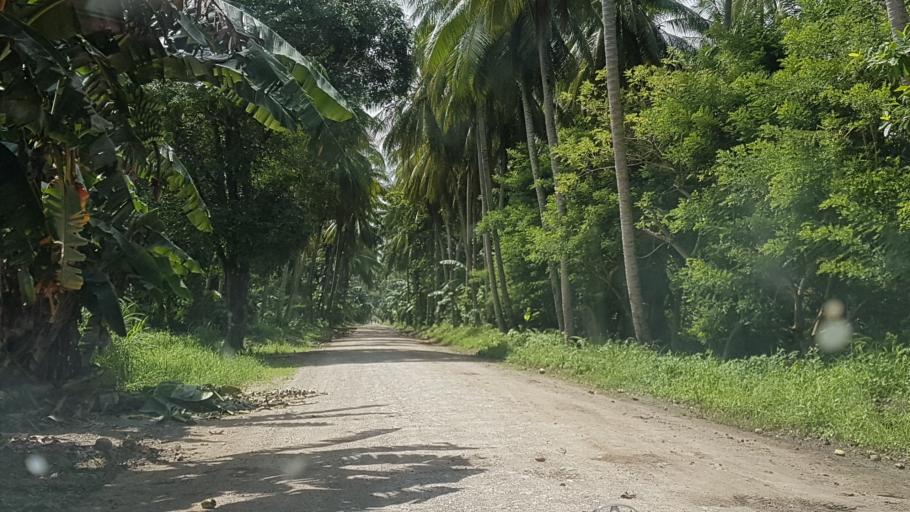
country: PG
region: East Sepik
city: Angoram
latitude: -4.2339
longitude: 144.9456
